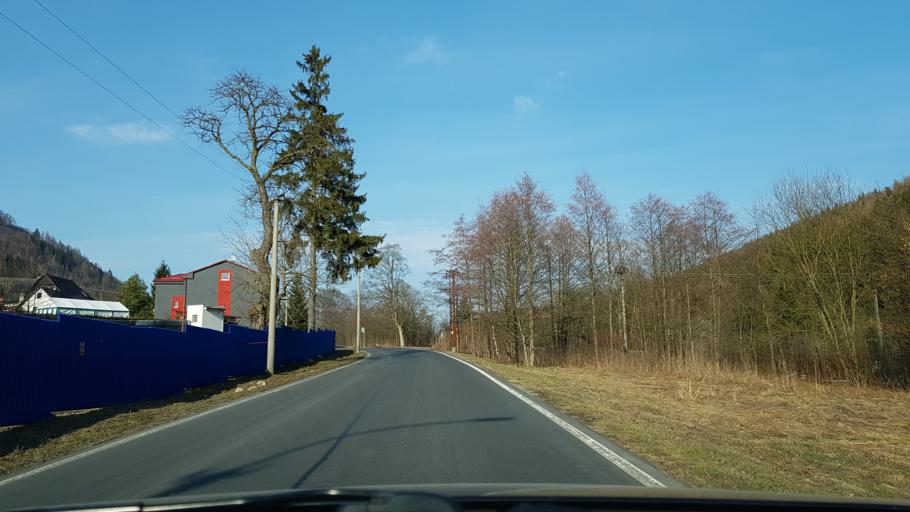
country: CZ
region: Olomoucky
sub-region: Okres Sumperk
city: Hanusovice
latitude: 50.0602
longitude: 16.9241
